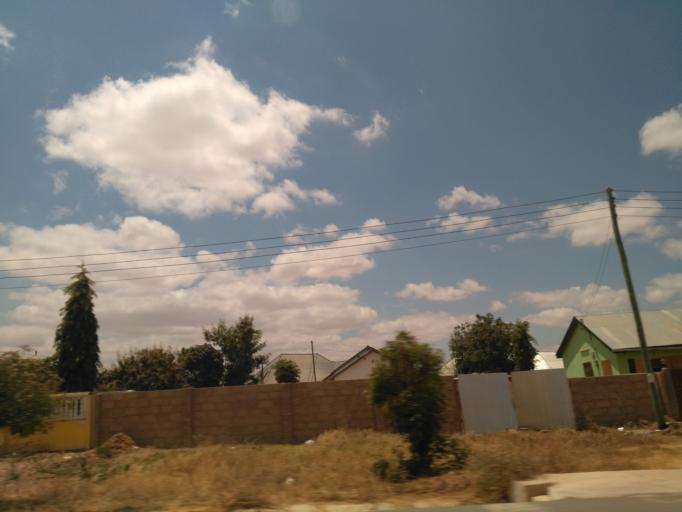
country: TZ
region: Dodoma
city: Kisasa
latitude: -6.1758
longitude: 35.7949
